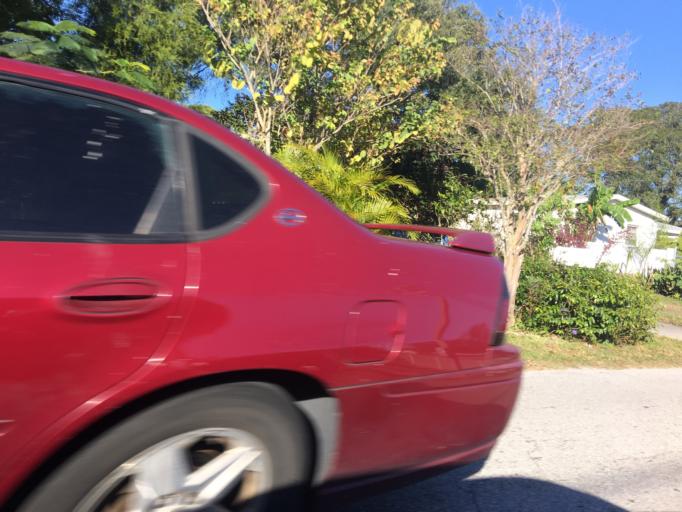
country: US
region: Florida
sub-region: Hillsborough County
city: Egypt Lake-Leto
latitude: 28.0181
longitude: -82.4909
